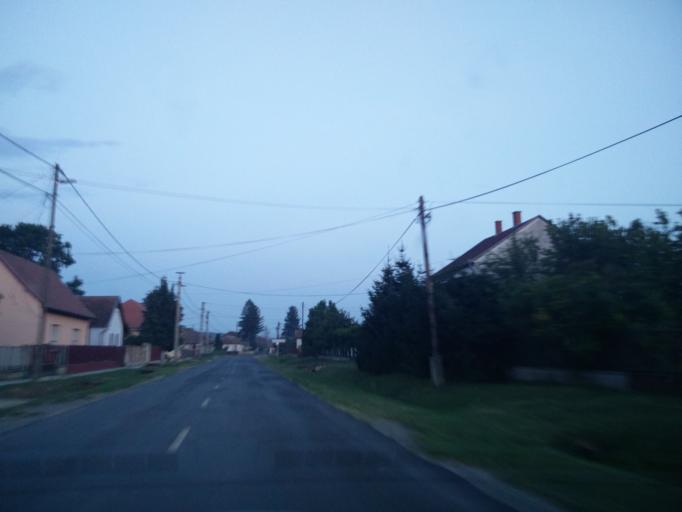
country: HU
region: Zala
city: Zalaegerszeg
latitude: 46.8862
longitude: 16.9197
